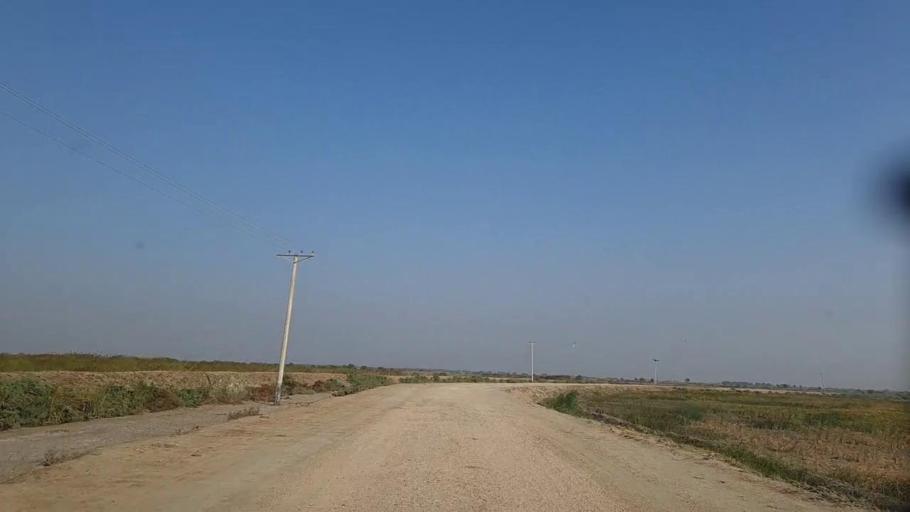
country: PK
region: Sindh
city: Jati
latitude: 24.4616
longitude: 68.2816
